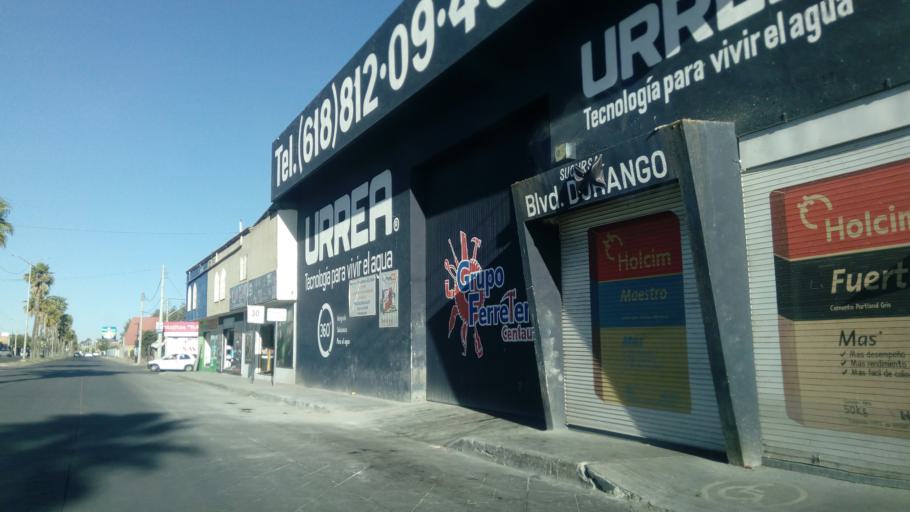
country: MX
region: Durango
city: Victoria de Durango
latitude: 24.0102
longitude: -104.6912
